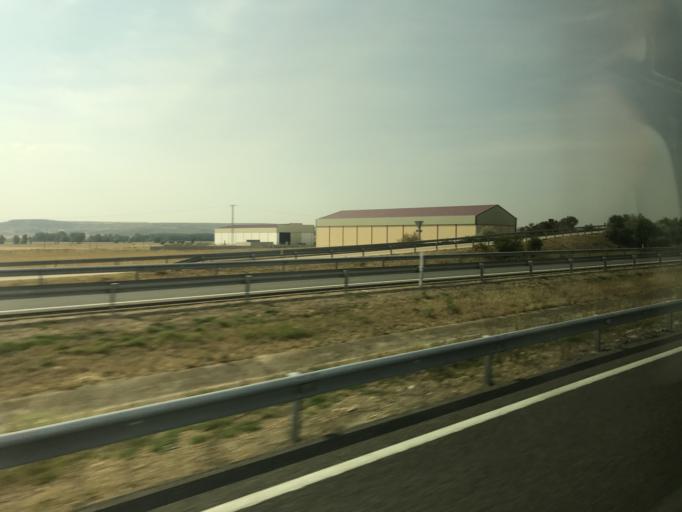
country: ES
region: Castille and Leon
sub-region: Provincia de Burgos
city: Villazopeque
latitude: 42.2046
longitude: -4.0169
